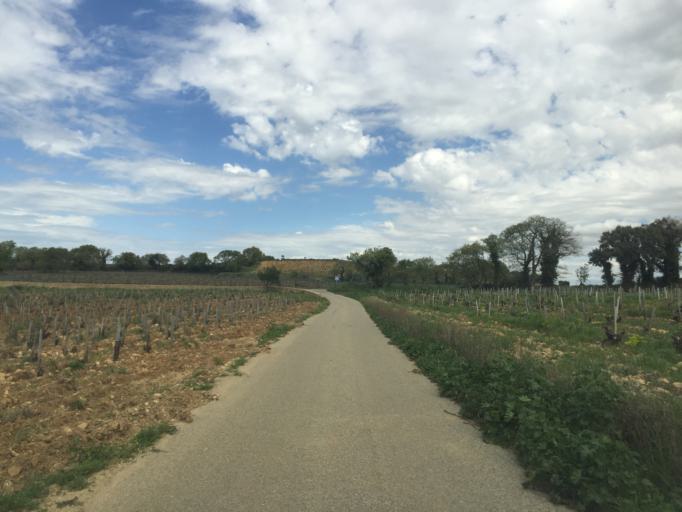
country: FR
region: Provence-Alpes-Cote d'Azur
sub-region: Departement du Vaucluse
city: Chateauneuf-du-Pape
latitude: 44.0565
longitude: 4.8543
